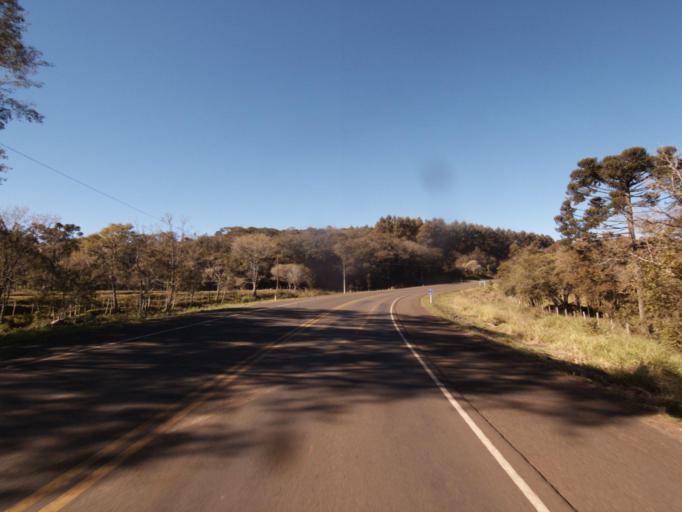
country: AR
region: Misiones
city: Bernardo de Irigoyen
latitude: -26.6697
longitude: -53.5769
